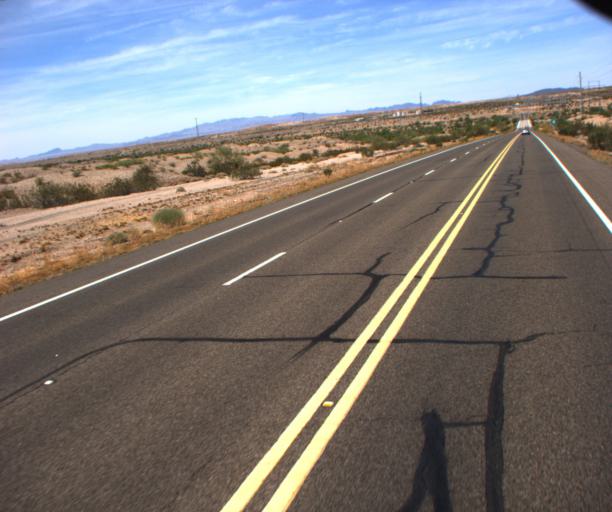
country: US
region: Arizona
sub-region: La Paz County
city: Parker
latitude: 33.9858
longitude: -114.2169
